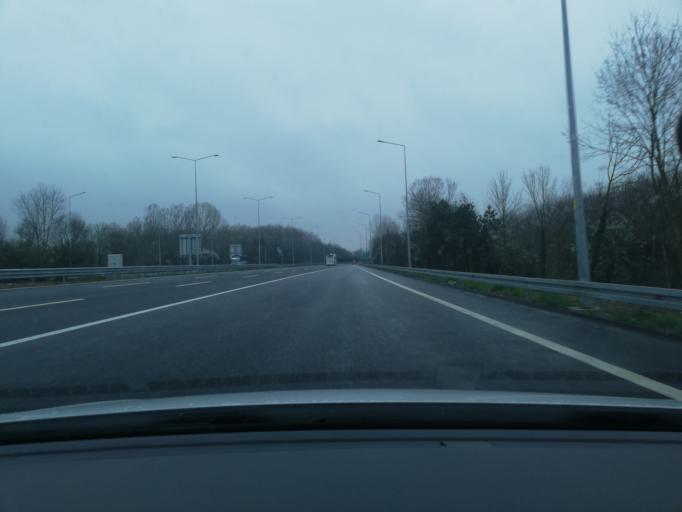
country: TR
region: Duzce
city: Duzce
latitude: 40.8052
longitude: 31.1588
